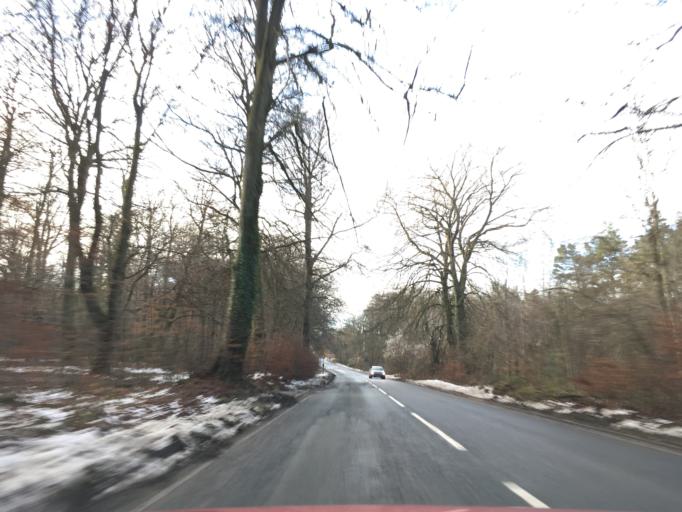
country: GB
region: England
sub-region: Gloucestershire
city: Coleford
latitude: 51.8113
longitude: -2.6022
